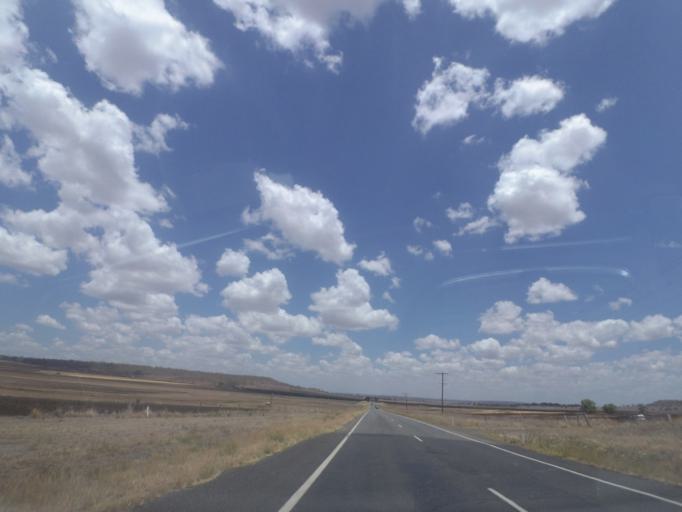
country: AU
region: Queensland
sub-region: Southern Downs
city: Warwick
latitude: -28.0003
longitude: 151.9935
